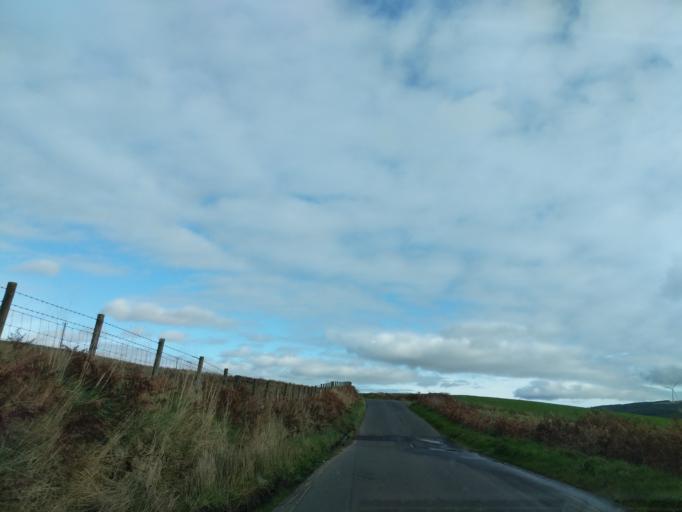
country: GB
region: Scotland
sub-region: Dumfries and Galloway
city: Castle Douglas
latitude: 55.1180
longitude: -4.0897
